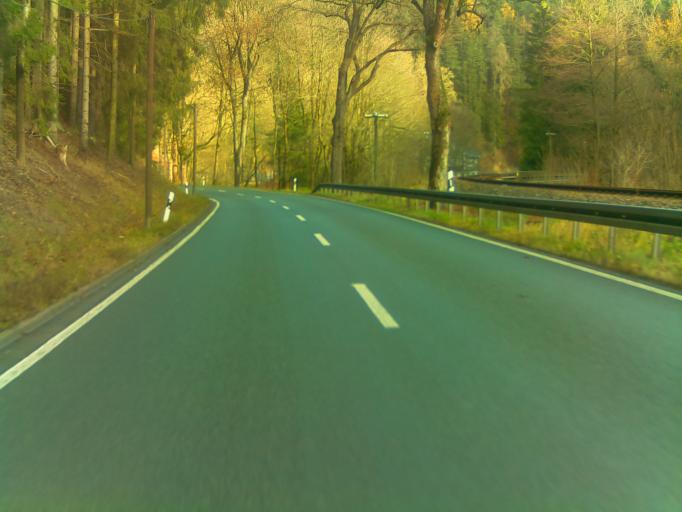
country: DE
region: Thuringia
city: Mellenbach-Glasbach
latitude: 50.6049
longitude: 11.0866
